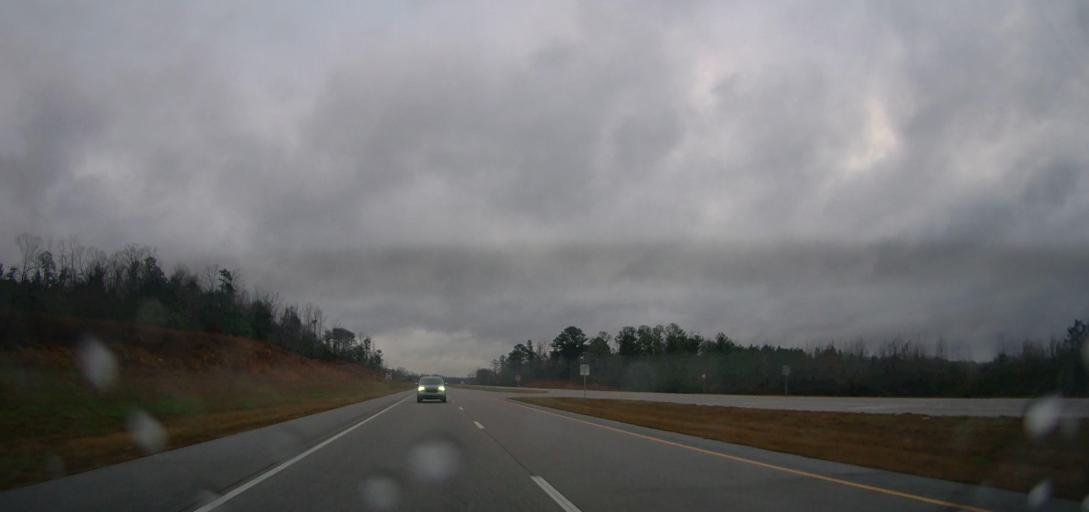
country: US
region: Alabama
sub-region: Bibb County
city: Centreville
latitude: 32.9449
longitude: -87.0879
